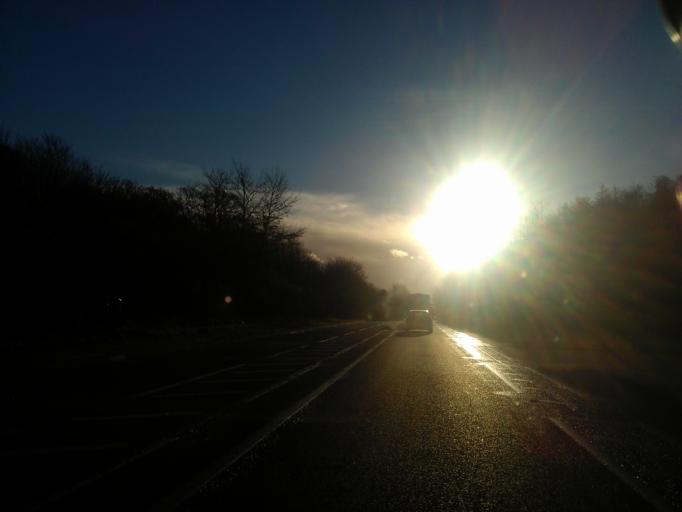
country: GB
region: England
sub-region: Essex
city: Little Clacton
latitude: 51.8455
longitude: 1.1073
